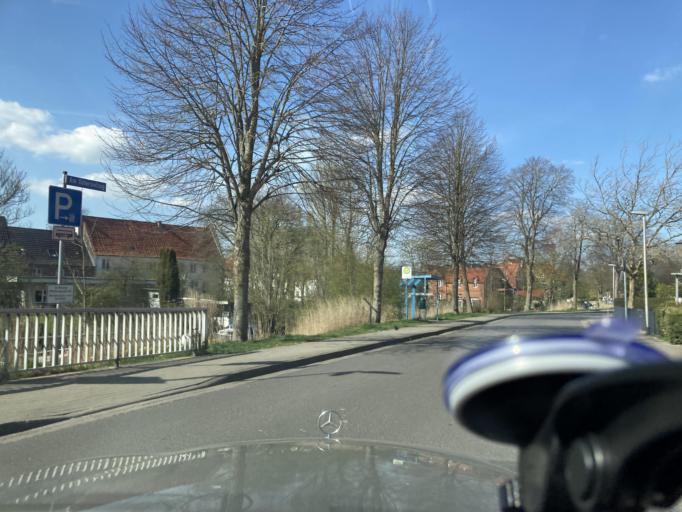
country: DE
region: Schleswig-Holstein
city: Friedrichstadt
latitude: 54.3753
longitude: 9.0915
